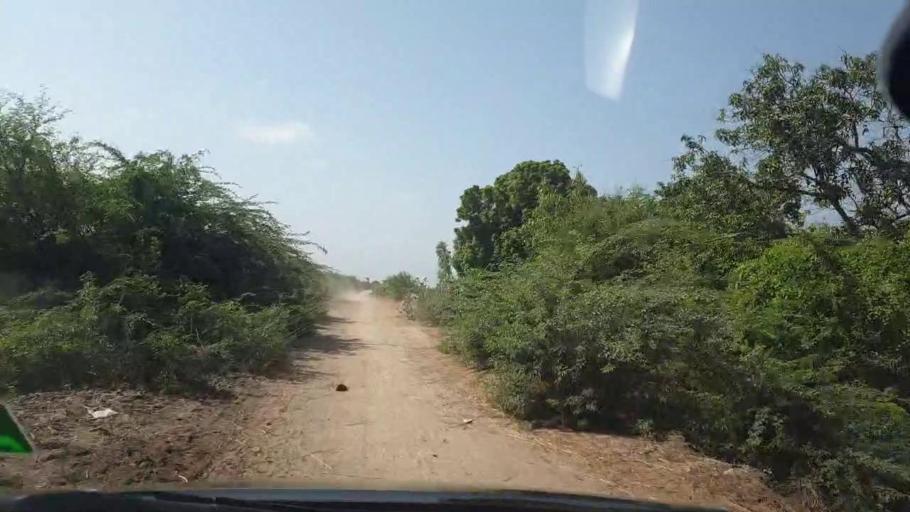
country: PK
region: Sindh
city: Tando Bago
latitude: 24.7670
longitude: 68.9441
